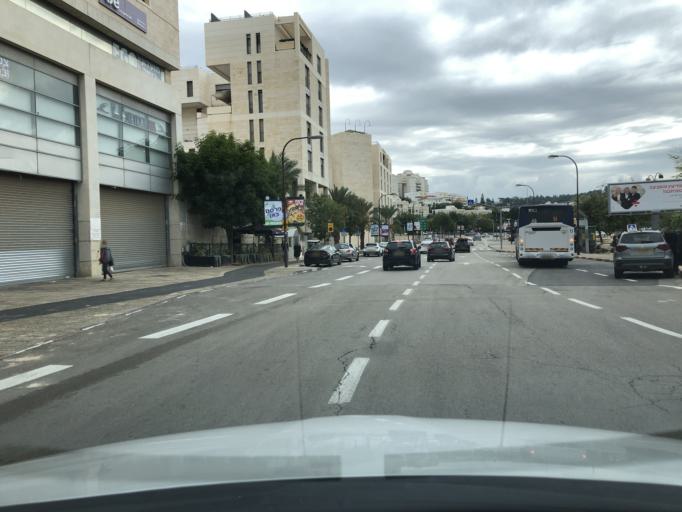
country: IL
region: Central District
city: Modiin
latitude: 31.8994
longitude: 35.0069
